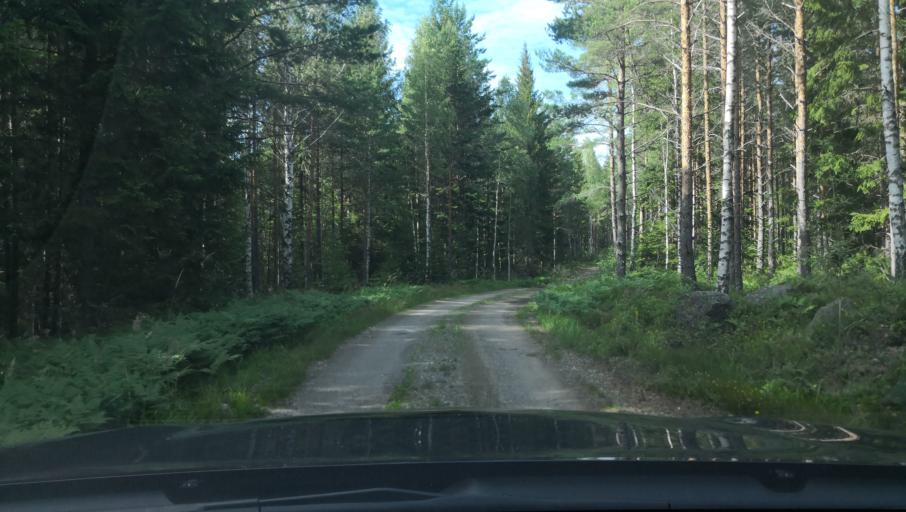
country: SE
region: Vaestmanland
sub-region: Surahammars Kommun
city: Surahammar
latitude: 59.6719
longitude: 16.1086
